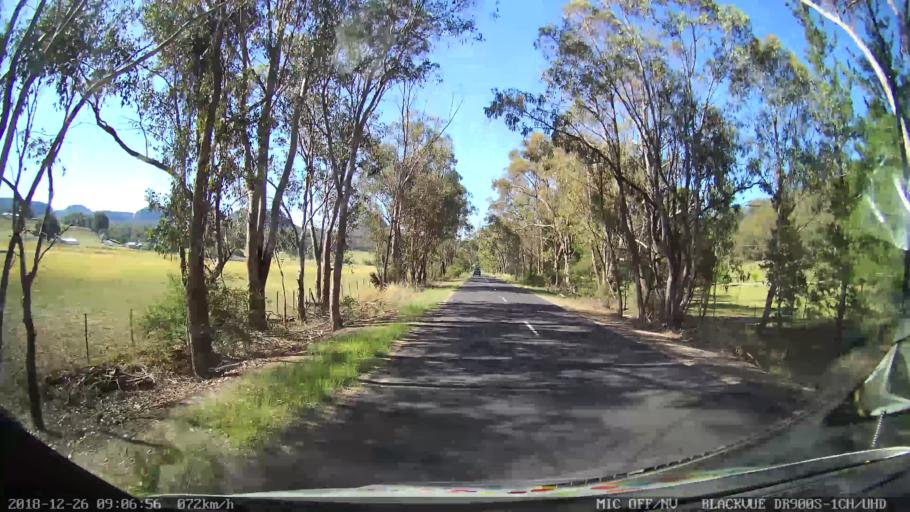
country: AU
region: New South Wales
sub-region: Mid-Western Regional
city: Kandos
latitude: -32.6999
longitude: 150.0054
